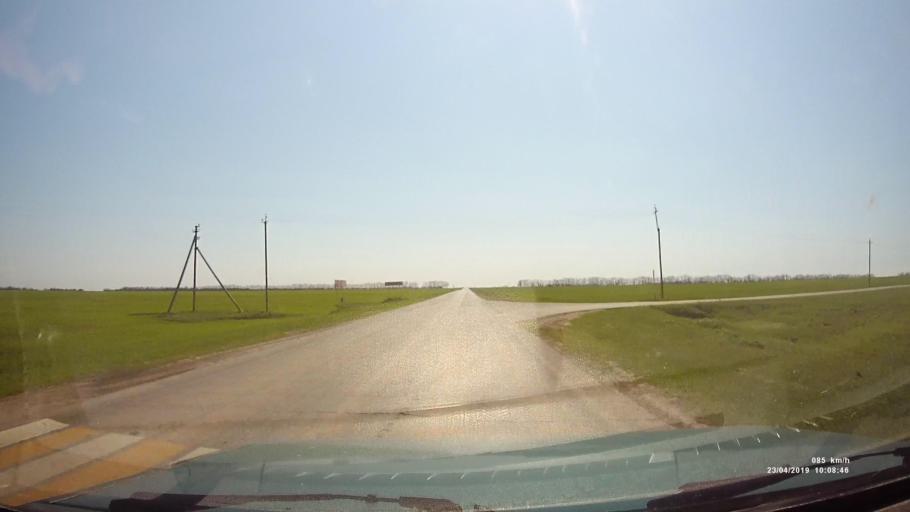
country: RU
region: Rostov
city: Sovetskoye
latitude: 46.7171
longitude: 42.2703
